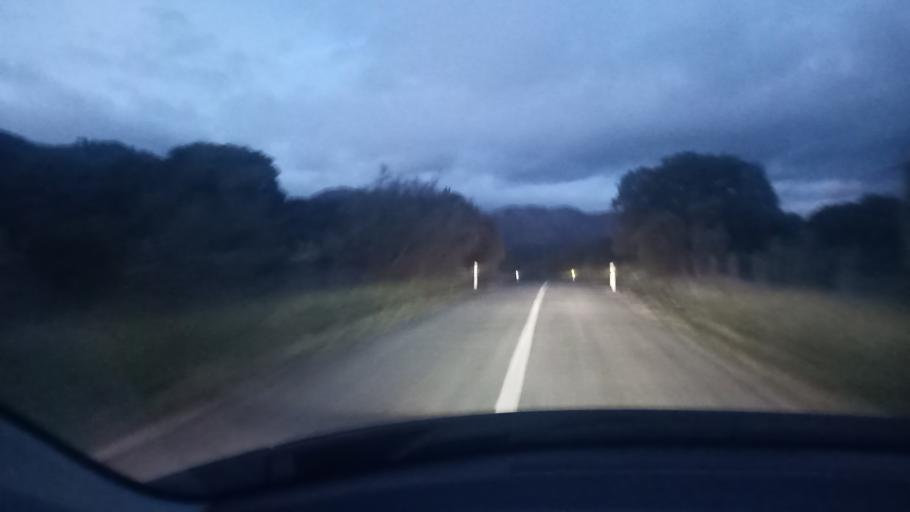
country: ES
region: Madrid
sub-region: Provincia de Madrid
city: Colmenar del Arroyo
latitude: 40.4376
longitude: -4.2428
